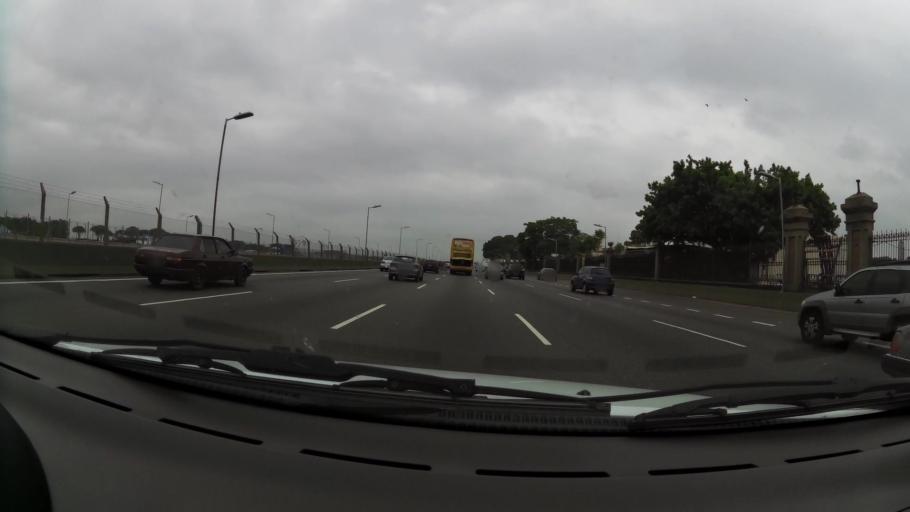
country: AR
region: Buenos Aires F.D.
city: Colegiales
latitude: -34.5530
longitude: -58.4304
